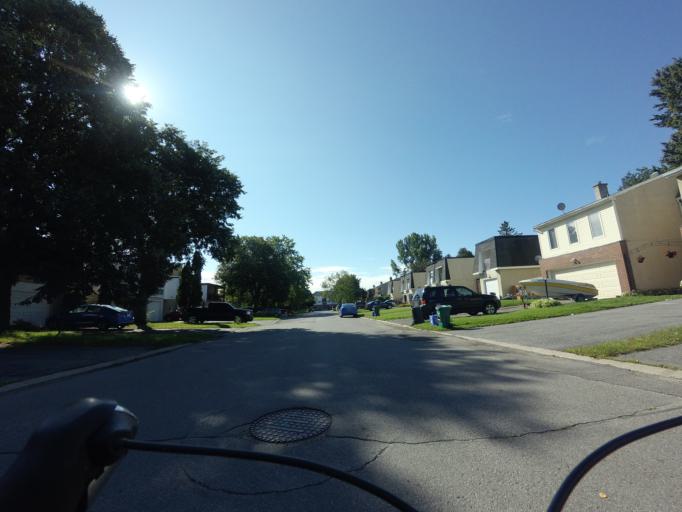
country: CA
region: Ontario
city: Bells Corners
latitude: 45.3174
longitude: -75.8324
